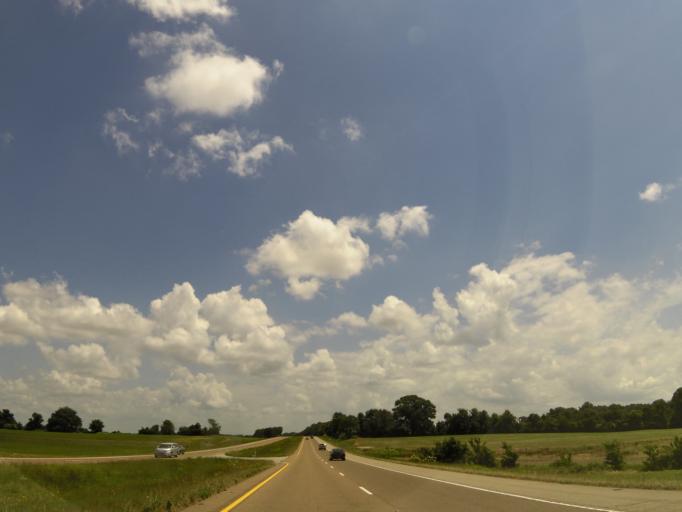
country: US
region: Tennessee
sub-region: Crockett County
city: Alamo
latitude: 35.7649
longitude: -89.1179
